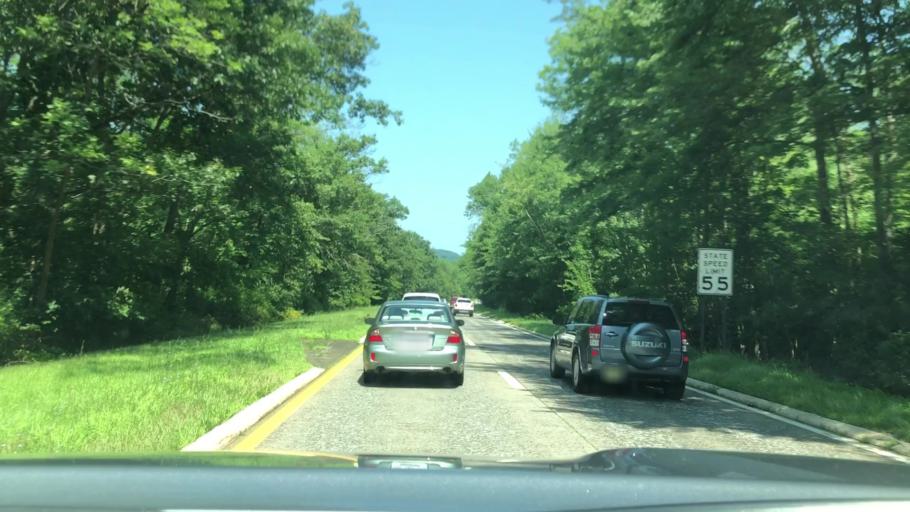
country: US
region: New York
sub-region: Rockland County
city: Pomona
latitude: 41.1749
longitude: -74.0347
